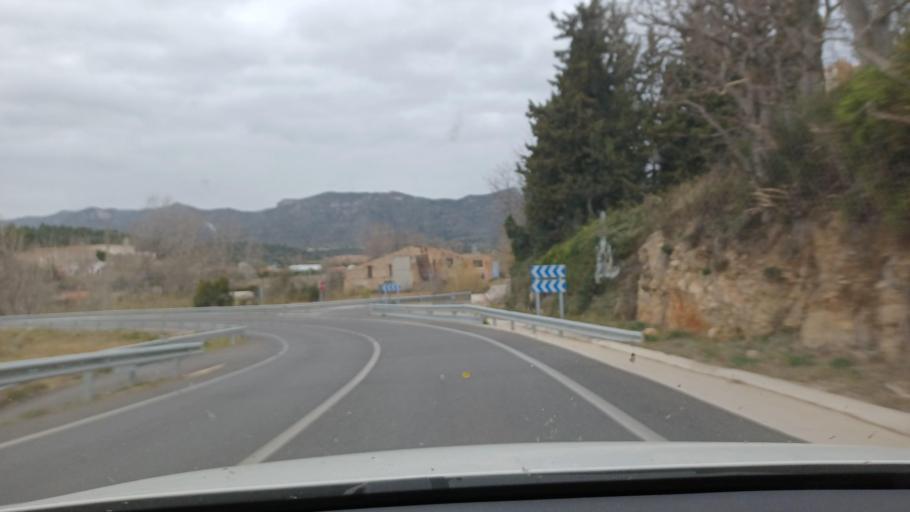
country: ES
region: Valencia
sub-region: Provincia de Castello
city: Rosell
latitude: 40.6335
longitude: 0.2786
